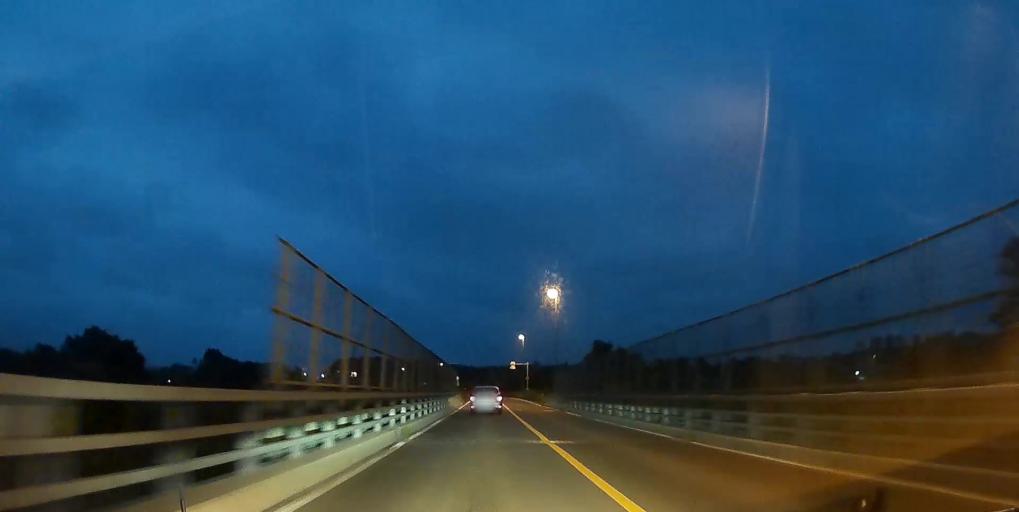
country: JP
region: Hokkaido
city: Nanae
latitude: 42.2101
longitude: 140.3950
